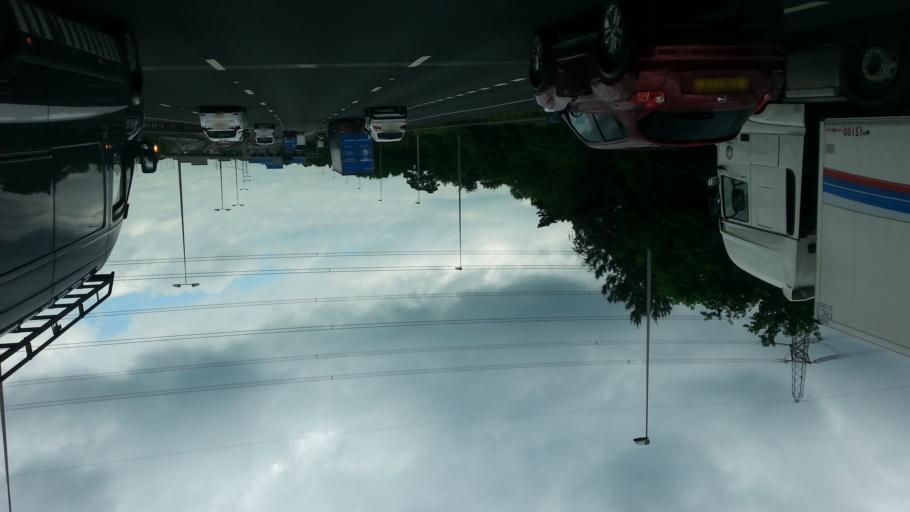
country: GB
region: England
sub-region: Warwickshire
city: Curdworth
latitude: 52.5245
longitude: -1.7286
